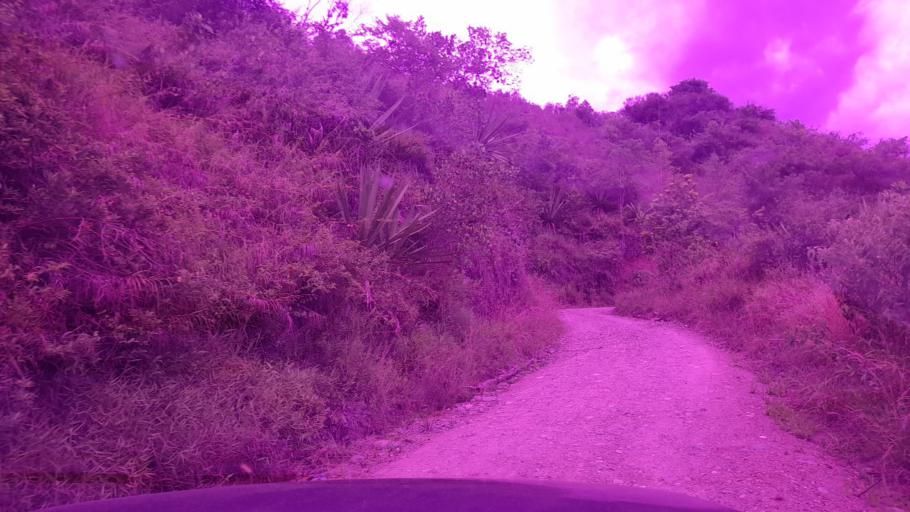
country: CO
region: Valle del Cauca
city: Andalucia
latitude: 4.1712
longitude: -76.1205
